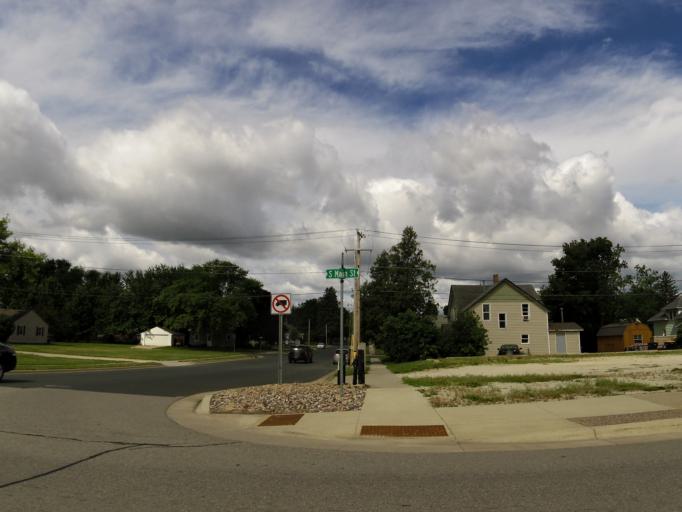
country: US
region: Minnesota
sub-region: Olmsted County
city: Stewartville
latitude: 43.8538
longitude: -92.4885
